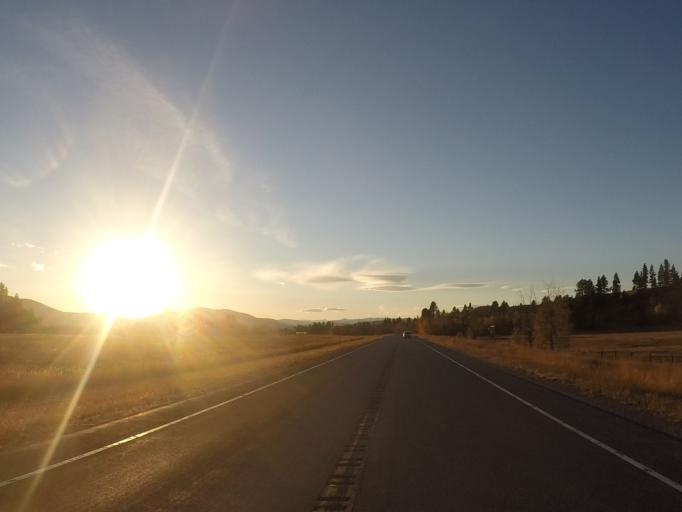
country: US
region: Montana
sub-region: Lewis and Clark County
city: Lincoln
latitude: 47.0163
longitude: -113.0743
